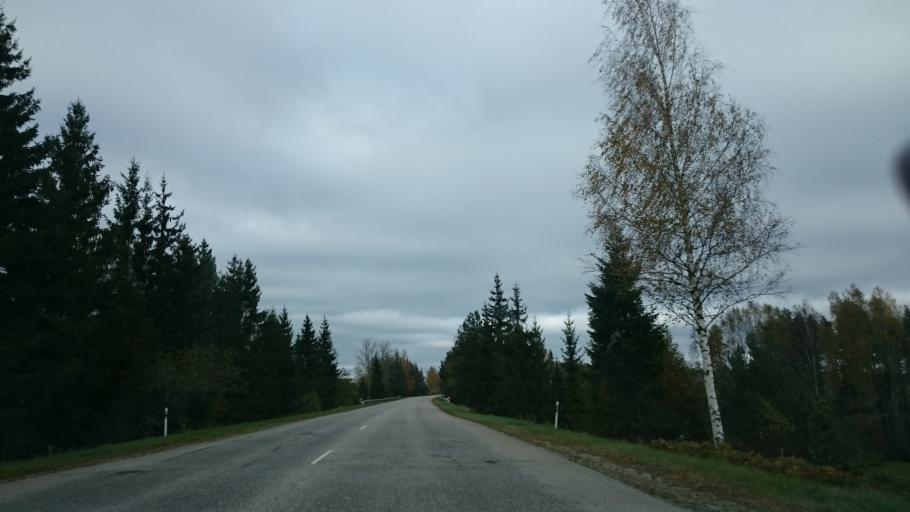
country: LV
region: Amatas Novads
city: Drabesi
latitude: 57.2307
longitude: 25.2540
